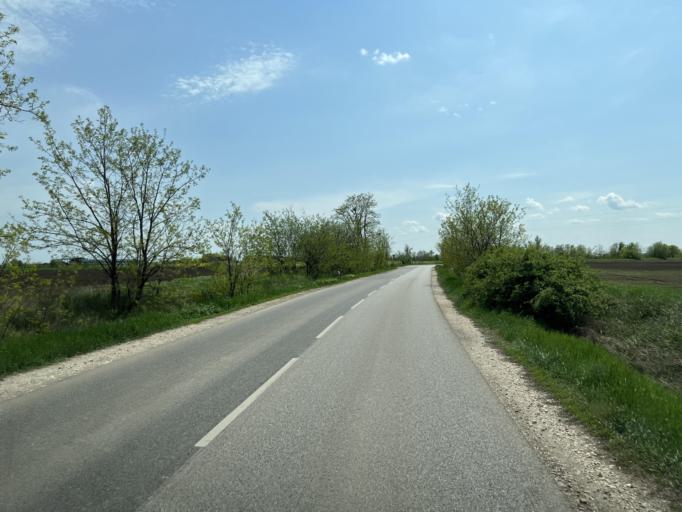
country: HU
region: Pest
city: Tapioszentmarton
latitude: 47.3077
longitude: 19.7610
